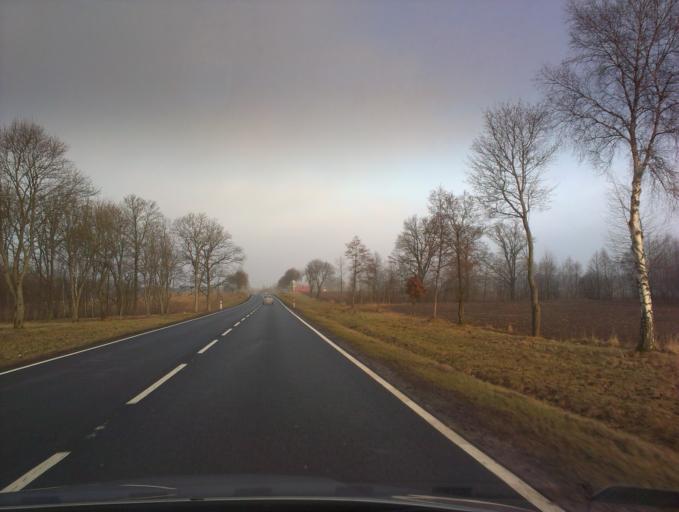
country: PL
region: West Pomeranian Voivodeship
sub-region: Powiat koszalinski
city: Bobolice
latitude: 54.0387
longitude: 16.4572
